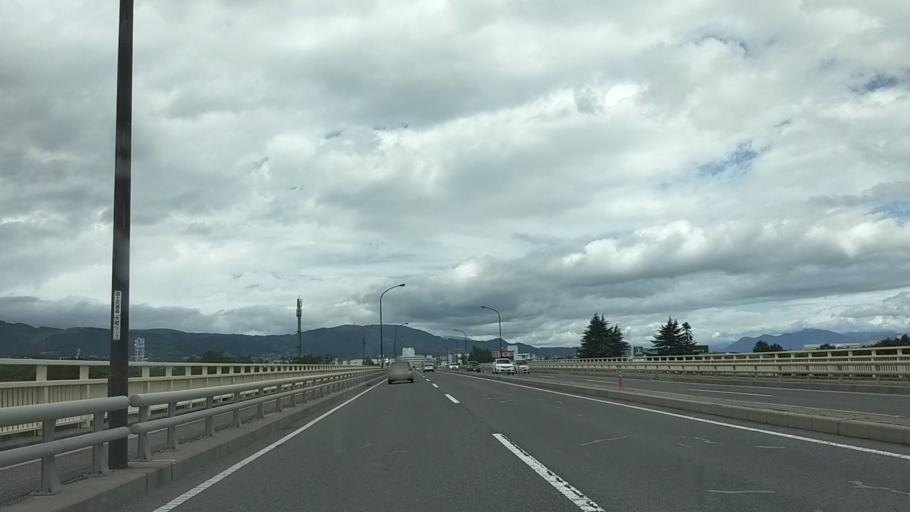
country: JP
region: Nagano
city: Nagano-shi
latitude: 36.6197
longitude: 138.1988
